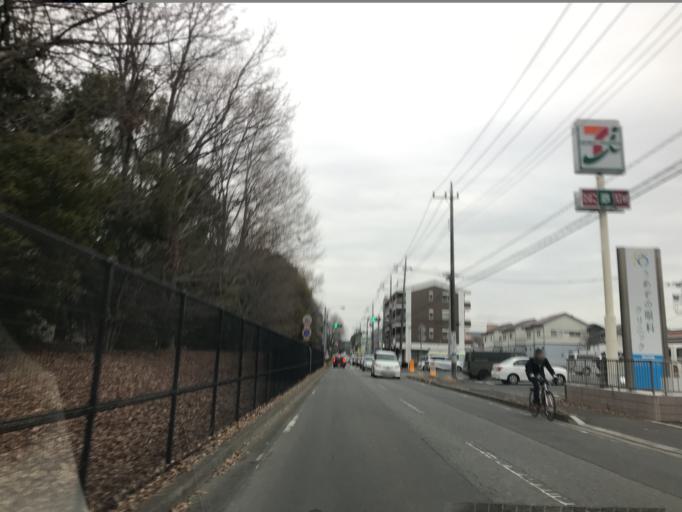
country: JP
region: Ibaraki
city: Naka
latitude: 36.0594
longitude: 140.1390
